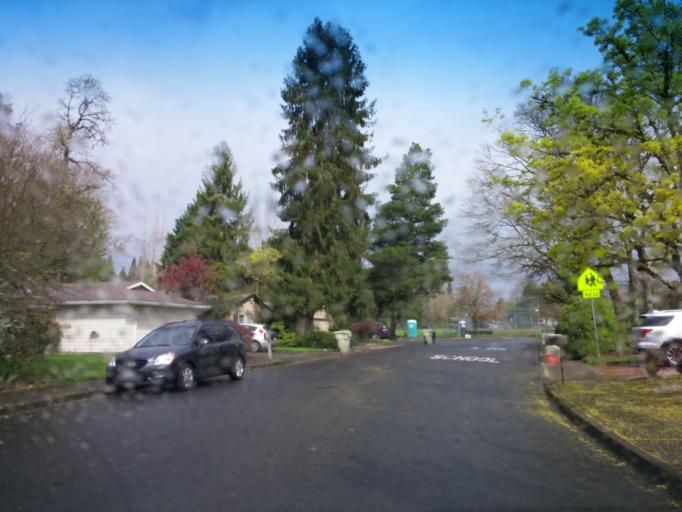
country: US
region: Oregon
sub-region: Washington County
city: Aloha
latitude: 45.5030
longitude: -122.8557
